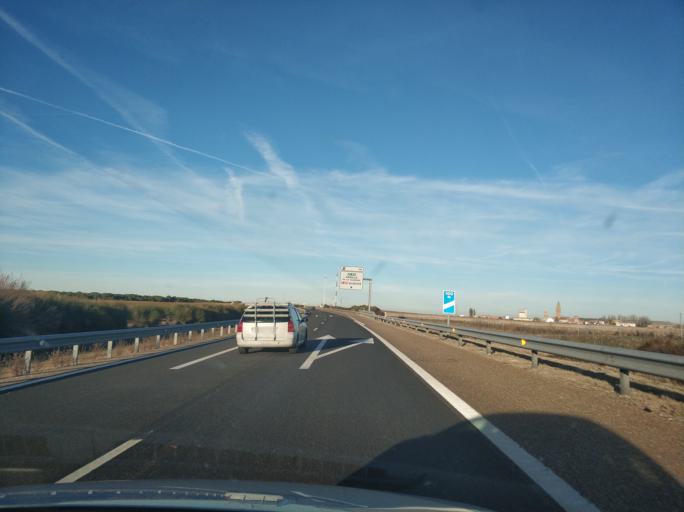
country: ES
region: Castille and Leon
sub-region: Provincia de Valladolid
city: Alaejos
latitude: 41.2975
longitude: -5.2319
